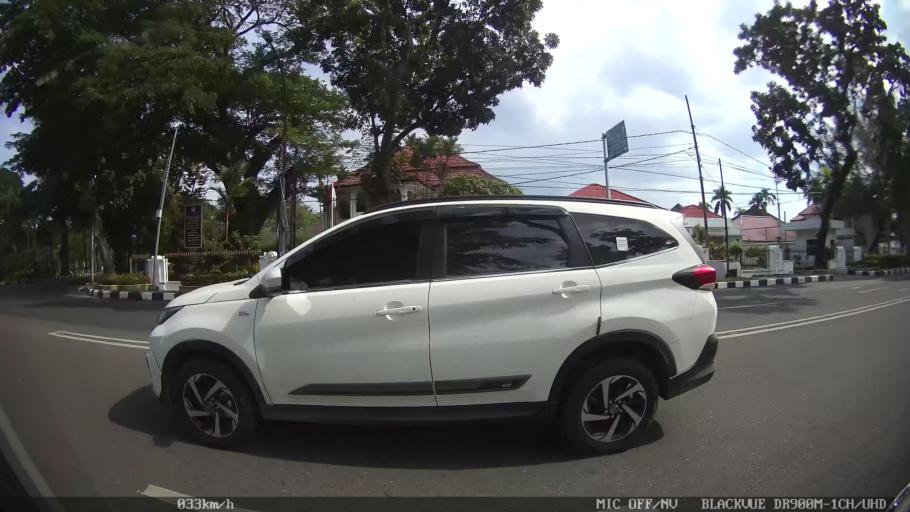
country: ID
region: North Sumatra
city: Medan
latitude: 3.5753
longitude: 98.6710
